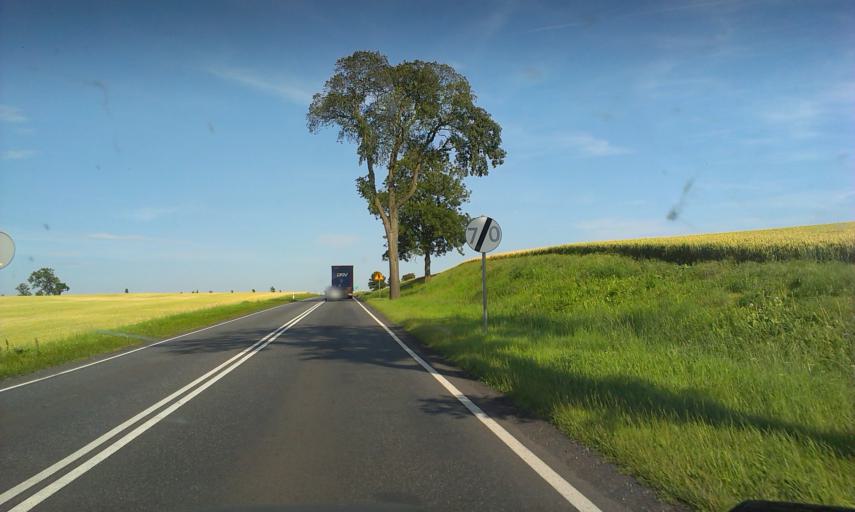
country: PL
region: Kujawsko-Pomorskie
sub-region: Powiat nakielski
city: Naklo nad Notecia
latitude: 53.1466
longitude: 17.5332
